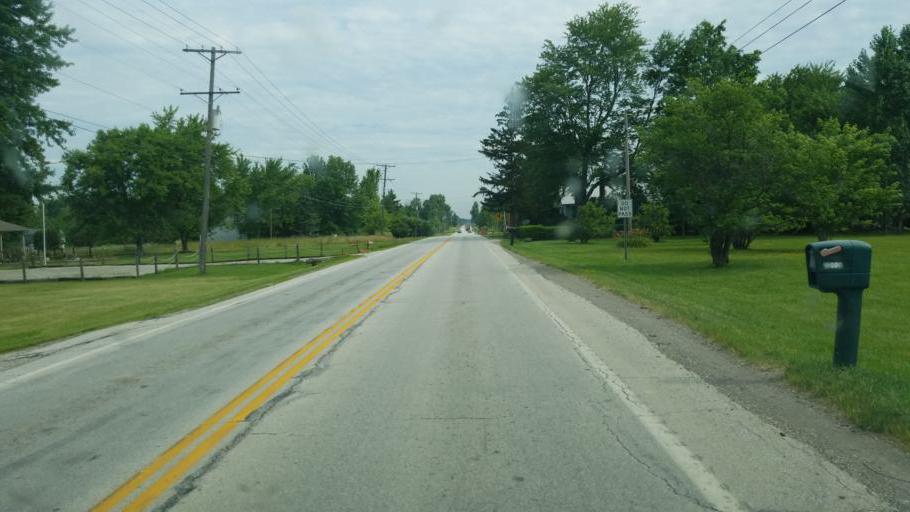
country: US
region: Ohio
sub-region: Lorain County
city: Eaton Estates
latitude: 41.2943
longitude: -82.0209
